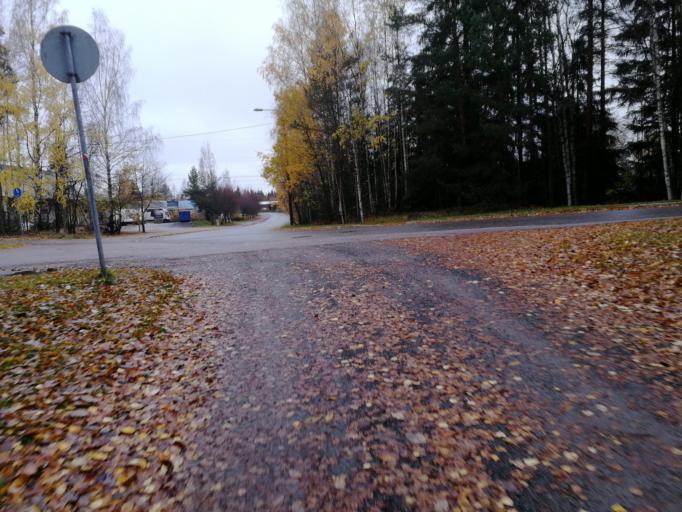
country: FI
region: Pirkanmaa
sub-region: Tampere
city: Tampere
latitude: 61.4572
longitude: 23.8702
